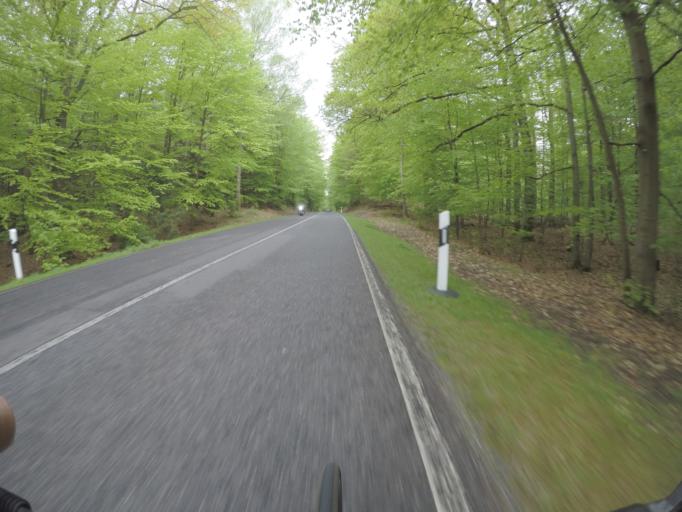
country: DE
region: Brandenburg
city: Joachimsthal
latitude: 52.9389
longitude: 13.7390
